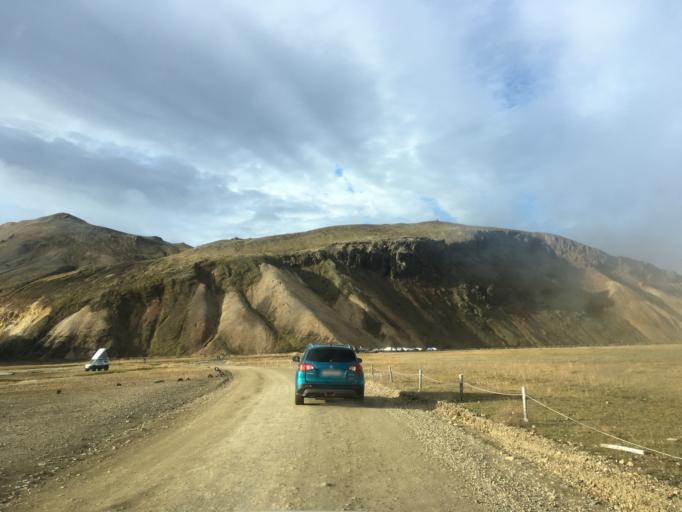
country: IS
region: South
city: Vestmannaeyjar
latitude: 63.9920
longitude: -19.0579
